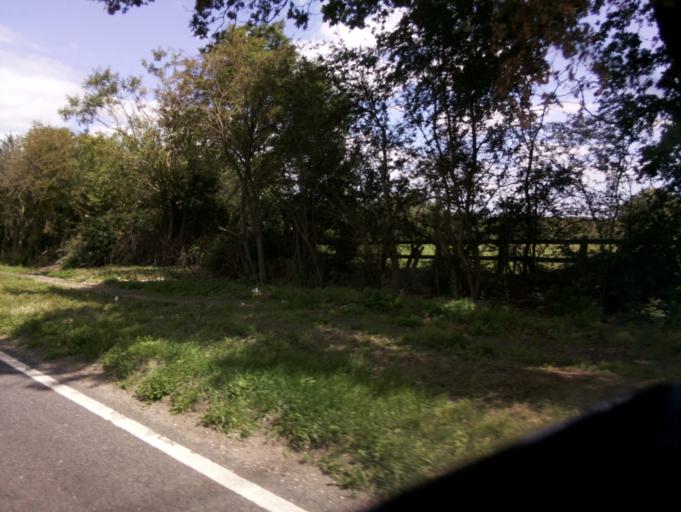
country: GB
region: England
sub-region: Buckinghamshire
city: Aylesbury
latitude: 51.8417
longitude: -0.8200
